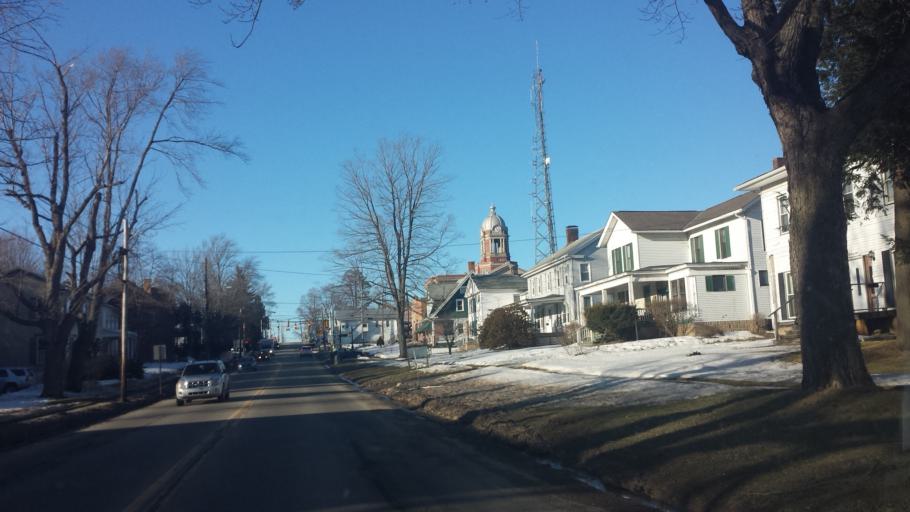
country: US
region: Pennsylvania
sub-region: Mercer County
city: Mercer
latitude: 41.2236
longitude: -80.2399
